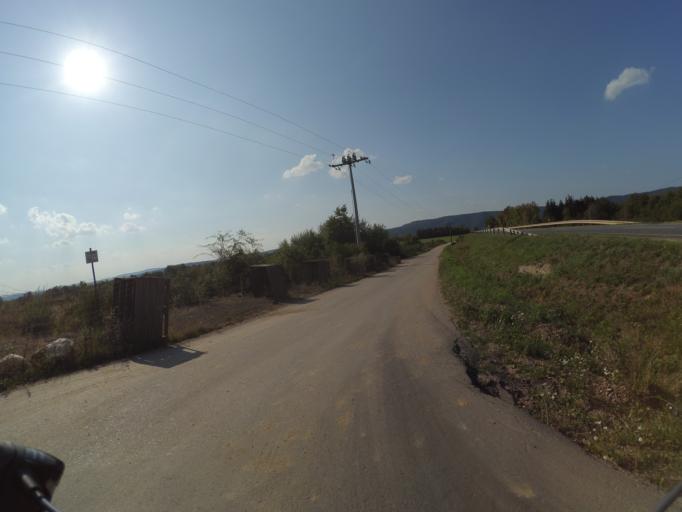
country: DE
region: Rheinland-Pfalz
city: Minheim
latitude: 49.8598
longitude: 6.9282
